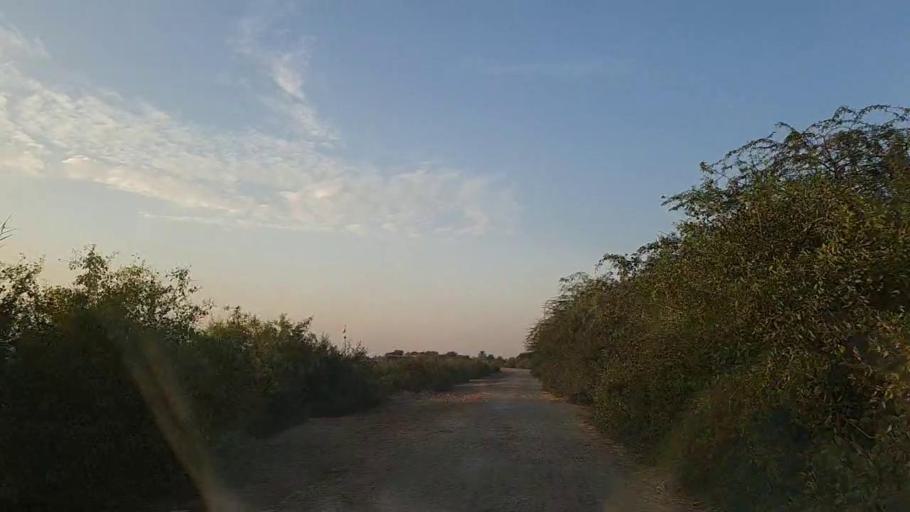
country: PK
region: Sindh
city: Chuhar Jamali
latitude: 24.4543
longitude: 68.1172
